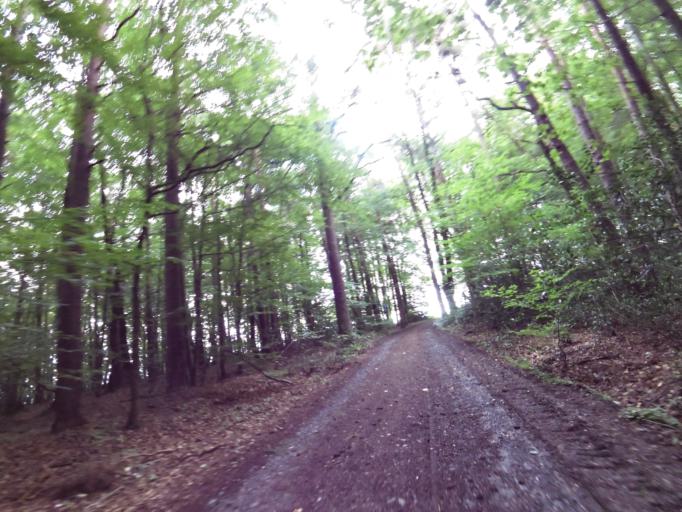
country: DE
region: Rheinland-Pfalz
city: Dernau
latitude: 50.5518
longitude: 7.0769
